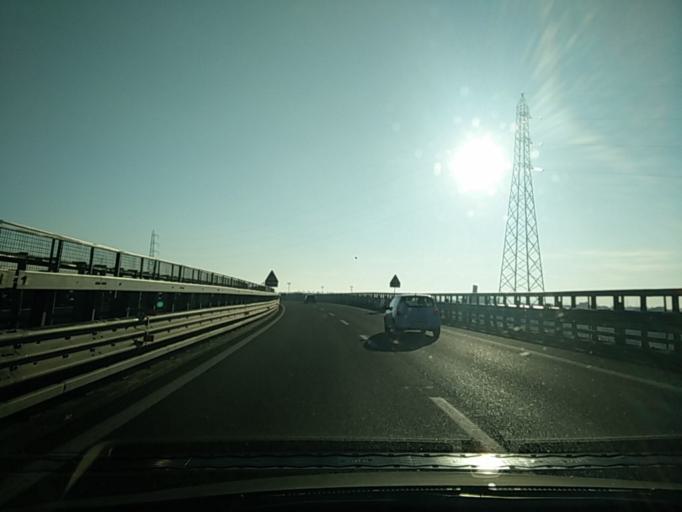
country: IT
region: Veneto
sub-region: Provincia di Padova
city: Vigodarzere
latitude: 45.4387
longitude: 11.8911
